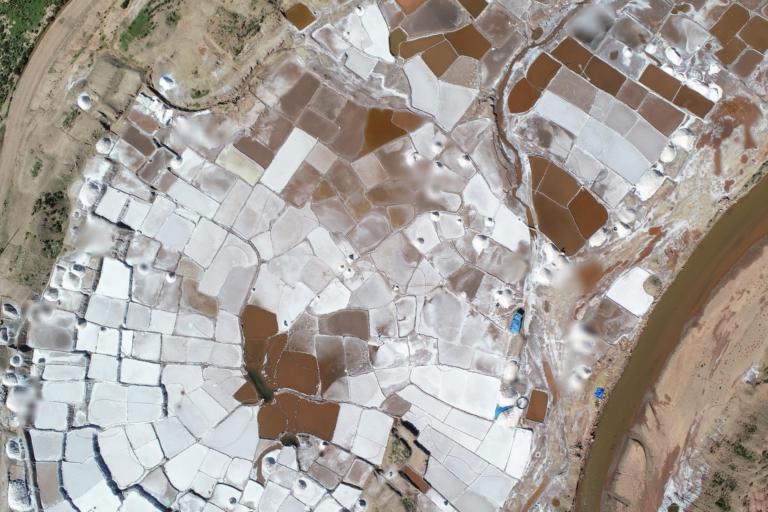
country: BO
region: La Paz
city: Patacamaya
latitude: -17.3003
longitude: -68.4848
